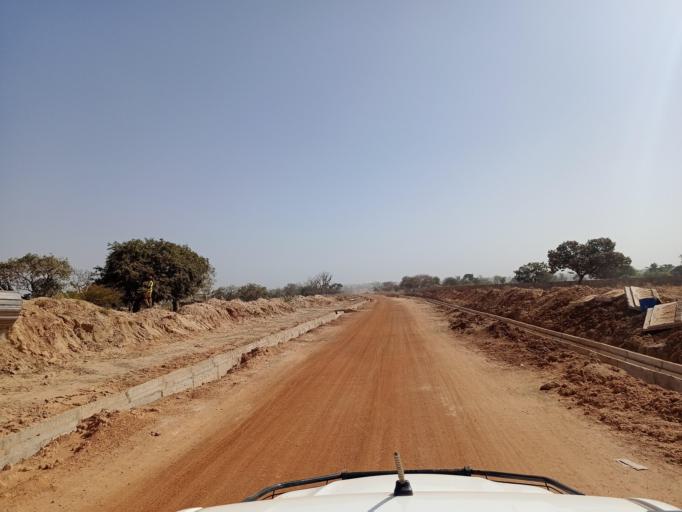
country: BF
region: Centre-Est
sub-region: Province du Boulgou
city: Garango
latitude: 11.5005
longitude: -0.5113
